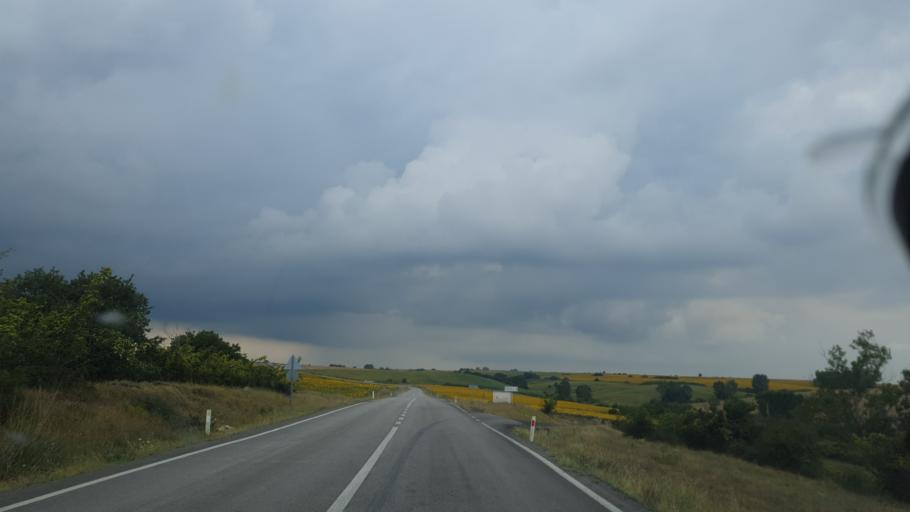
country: TR
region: Tekirdag
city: Hayrabolu
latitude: 41.2212
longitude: 27.0068
